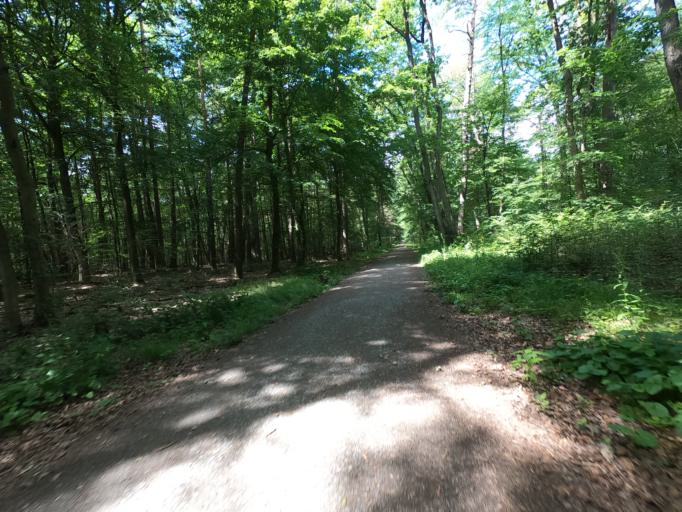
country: DE
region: Hesse
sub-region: Regierungsbezirk Darmstadt
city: Dietzenbach
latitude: 50.0277
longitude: 8.7738
